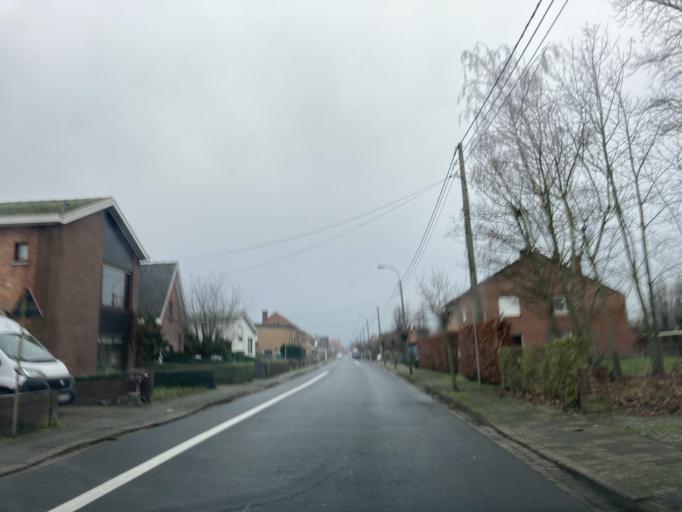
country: BE
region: Flanders
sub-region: Provincie West-Vlaanderen
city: Ichtegem
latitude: 51.1343
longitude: 3.0335
